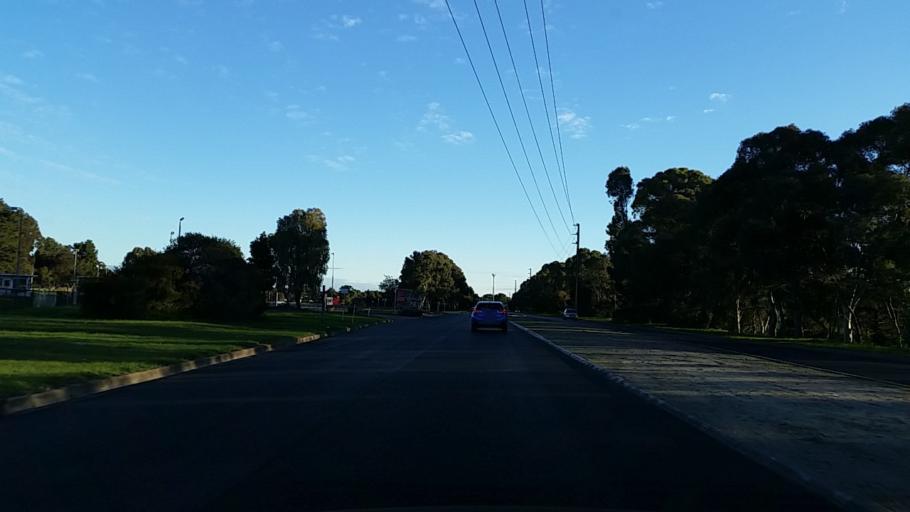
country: AU
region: South Australia
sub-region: Salisbury
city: Salisbury
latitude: -34.7456
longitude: 138.6475
